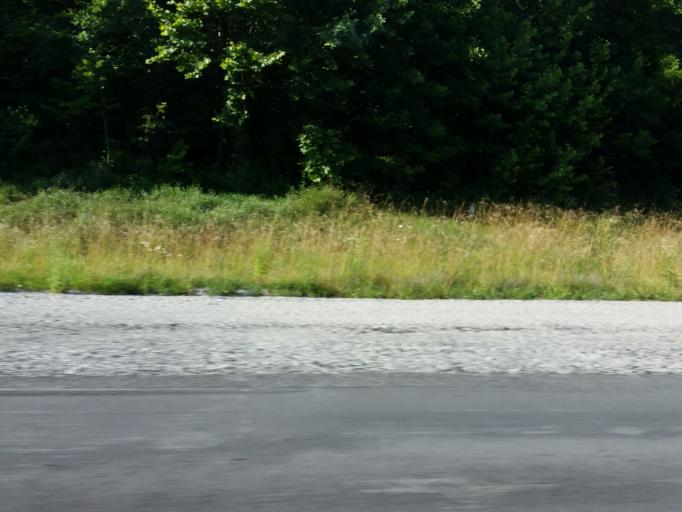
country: US
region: Tennessee
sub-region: Maury County
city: Mount Pleasant
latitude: 35.5637
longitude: -87.3618
